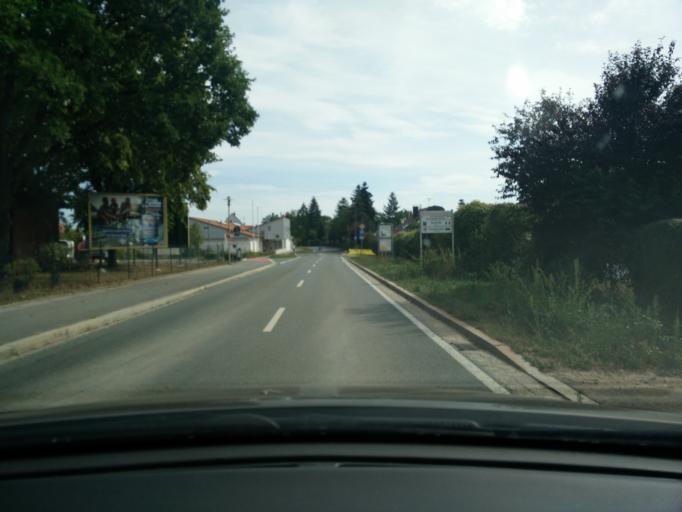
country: DE
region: Bavaria
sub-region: Regierungsbezirk Mittelfranken
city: Veitsbronn
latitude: 49.5139
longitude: 10.8711
